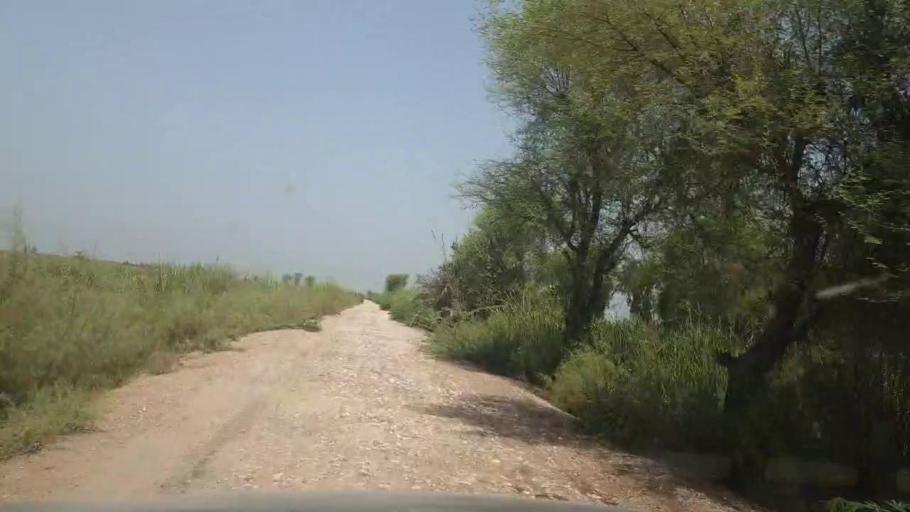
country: PK
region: Sindh
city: Lakhi
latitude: 27.8378
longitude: 68.6255
